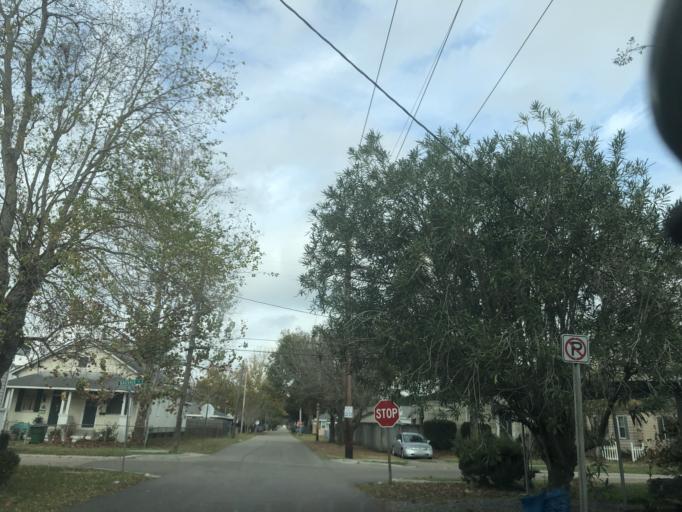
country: US
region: Louisiana
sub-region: Jefferson Parish
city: Metairie Terrace
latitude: 29.9766
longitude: -90.1615
